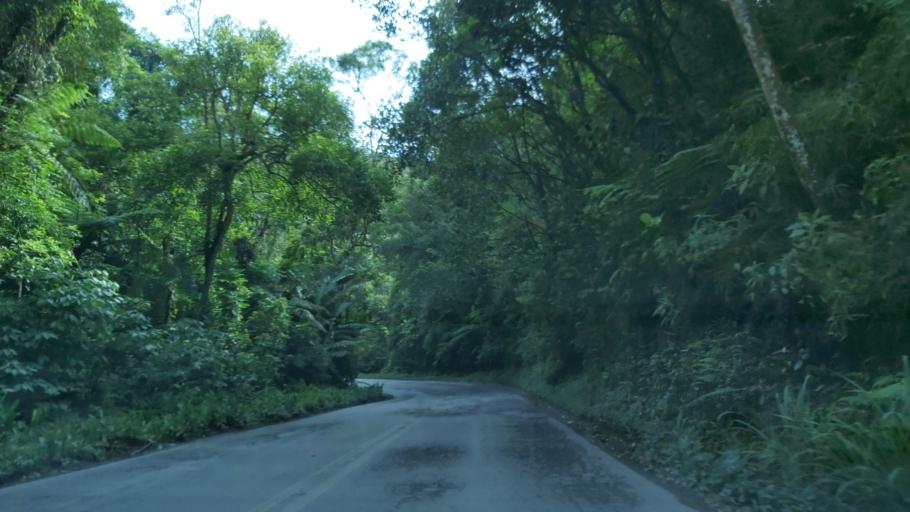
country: BR
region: Sao Paulo
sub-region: Miracatu
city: Miracatu
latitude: -24.0327
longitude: -47.5587
